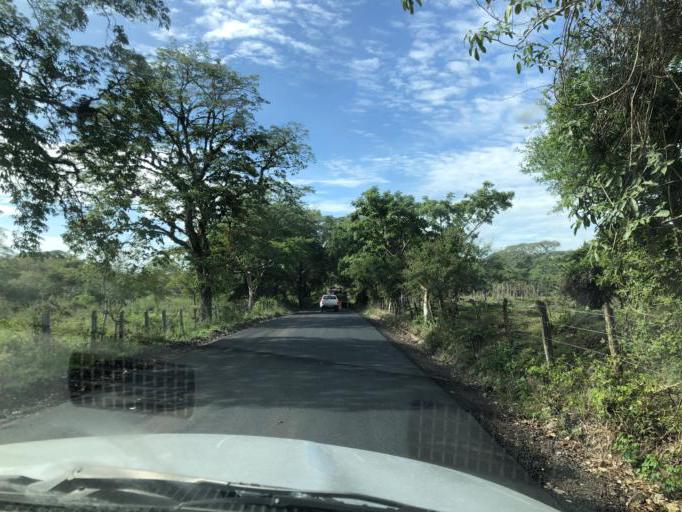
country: MX
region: Veracruz
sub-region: Alto Lucero de Gutierrez Barrios
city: Palma Sola
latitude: 19.8096
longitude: -96.5438
